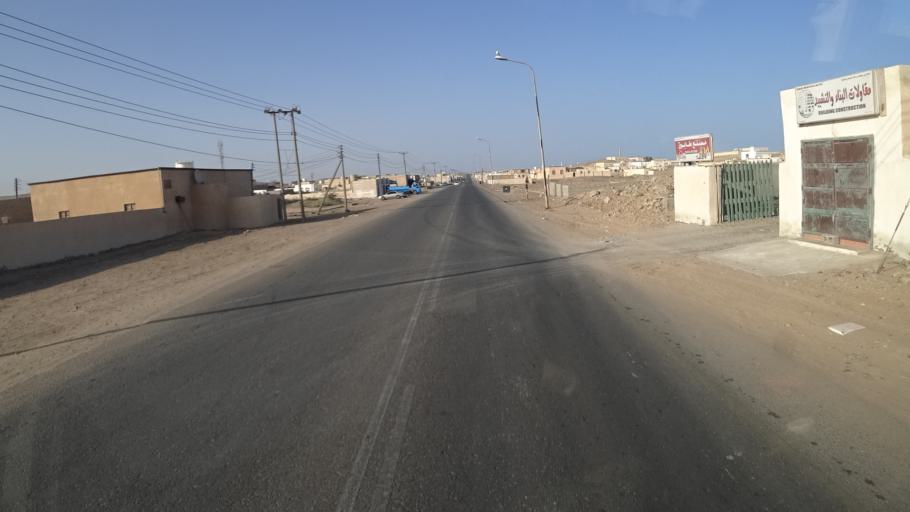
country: OM
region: Ash Sharqiyah
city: Sur
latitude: 22.1731
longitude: 59.7599
